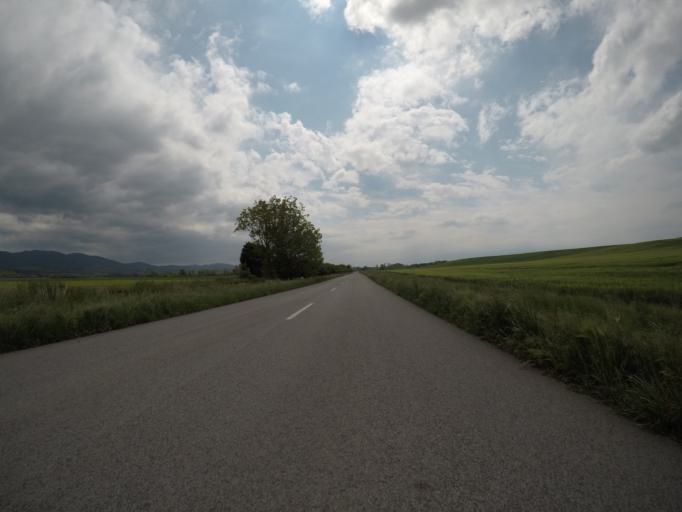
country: SK
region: Nitriansky
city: Zeliezovce
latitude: 48.0095
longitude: 18.7966
